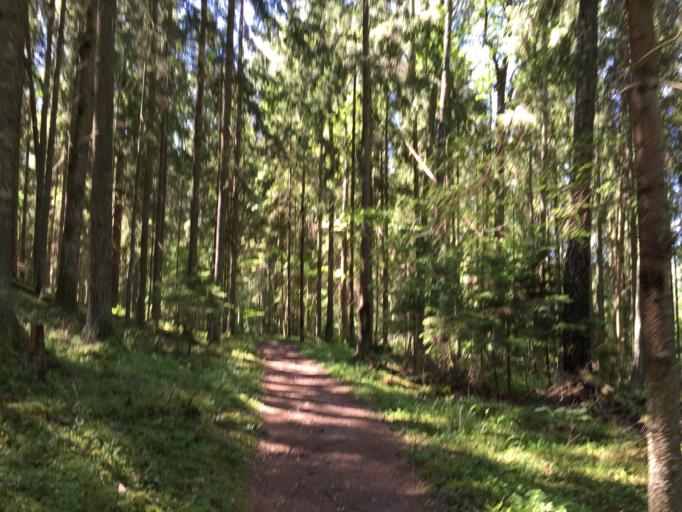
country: LV
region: Sigulda
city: Sigulda
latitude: 57.2197
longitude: 24.9061
